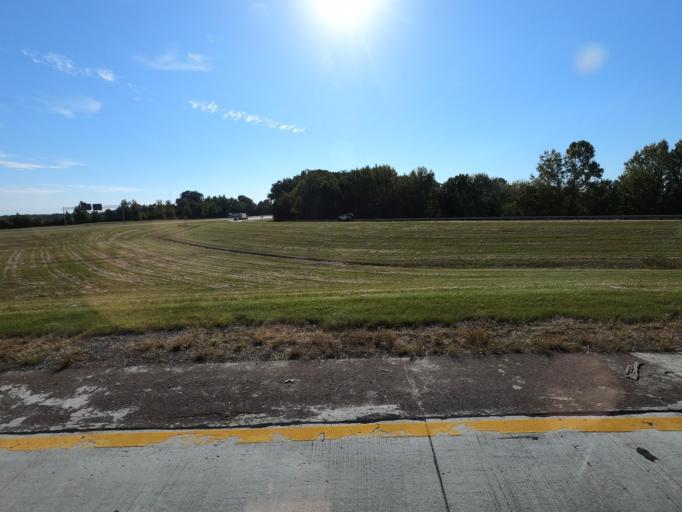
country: US
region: Tennessee
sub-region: Dyer County
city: Dyersburg
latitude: 36.0729
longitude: -89.3505
